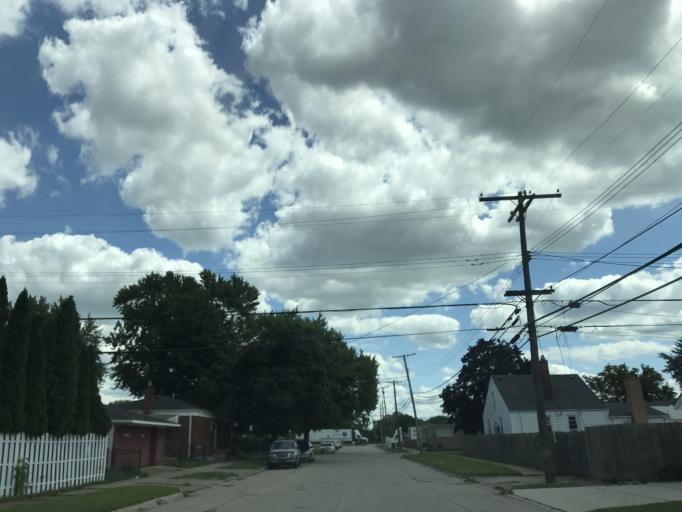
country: US
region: Michigan
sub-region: Wayne County
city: Melvindale
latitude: 42.2906
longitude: -83.1828
